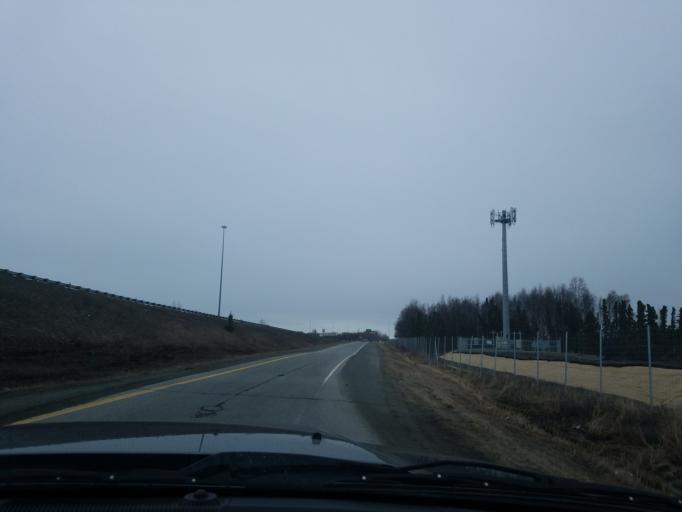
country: US
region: Alaska
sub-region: Anchorage Municipality
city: Anchorage
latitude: 61.1597
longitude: -149.9119
